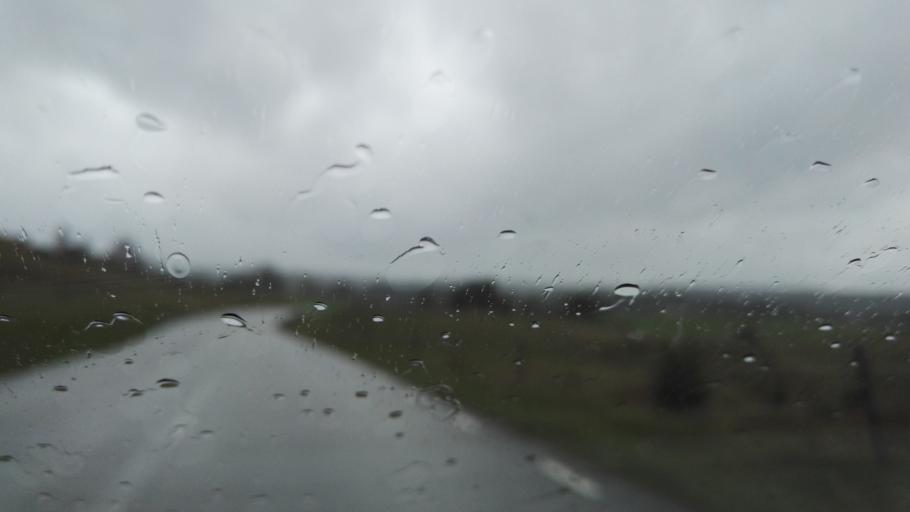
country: SE
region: Skane
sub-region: Kristianstads Kommun
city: Degeberga
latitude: 55.7220
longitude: 14.1171
